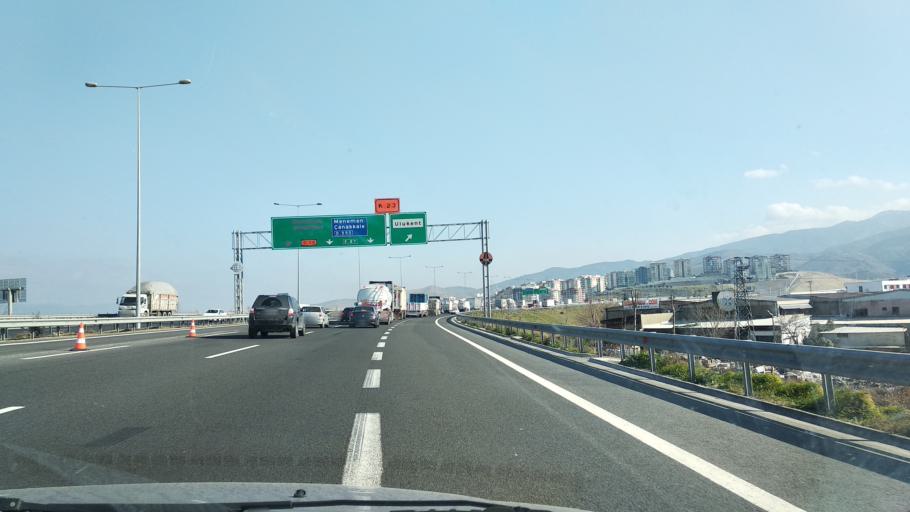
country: TR
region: Izmir
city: Menemen
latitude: 38.5703
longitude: 27.0493
